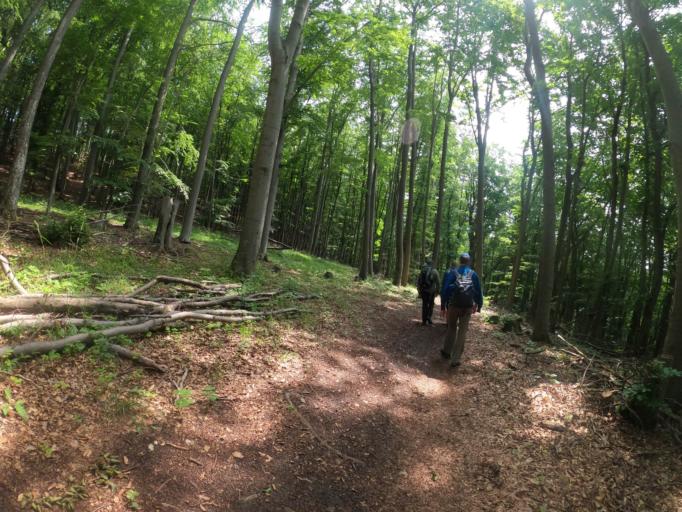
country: DE
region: Bavaria
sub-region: Upper Franconia
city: Litzendorf
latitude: 49.9253
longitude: 11.0568
